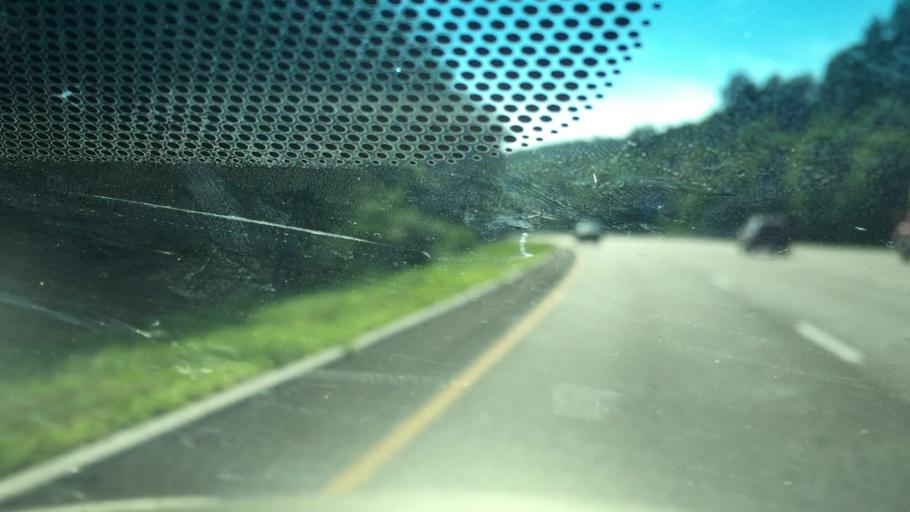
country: US
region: New Jersey
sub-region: Morris County
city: Budd Lake
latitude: 40.9253
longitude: -74.7862
